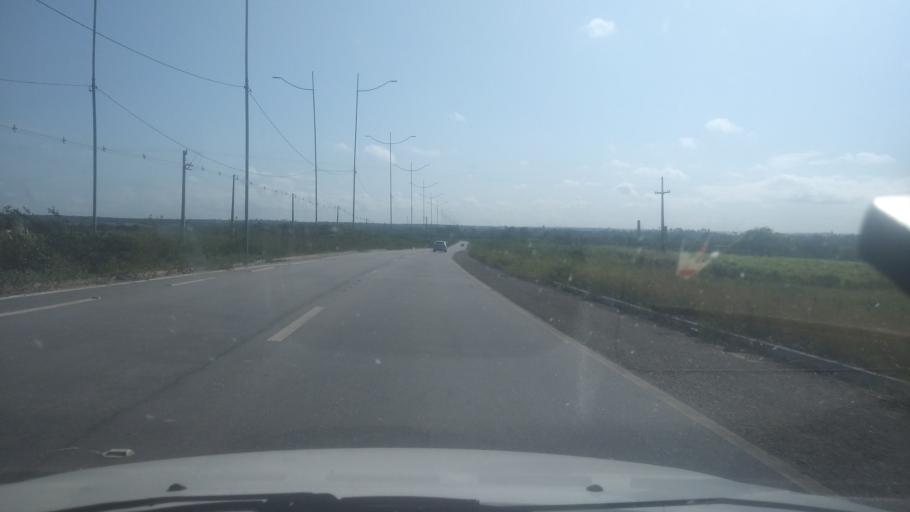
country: BR
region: Rio Grande do Norte
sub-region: Macaiba
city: Macaiba
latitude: -5.8198
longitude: -35.3658
